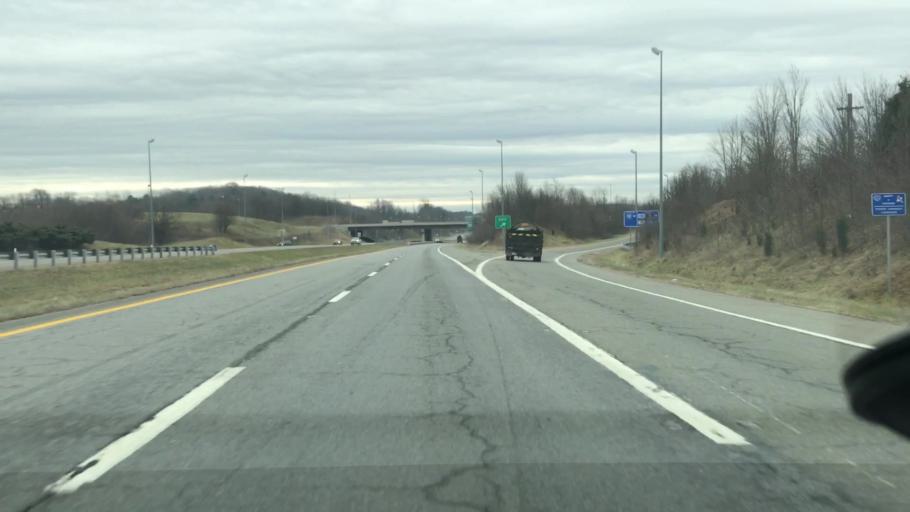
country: US
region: Virginia
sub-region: Montgomery County
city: Merrimac
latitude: 37.1678
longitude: -80.4160
